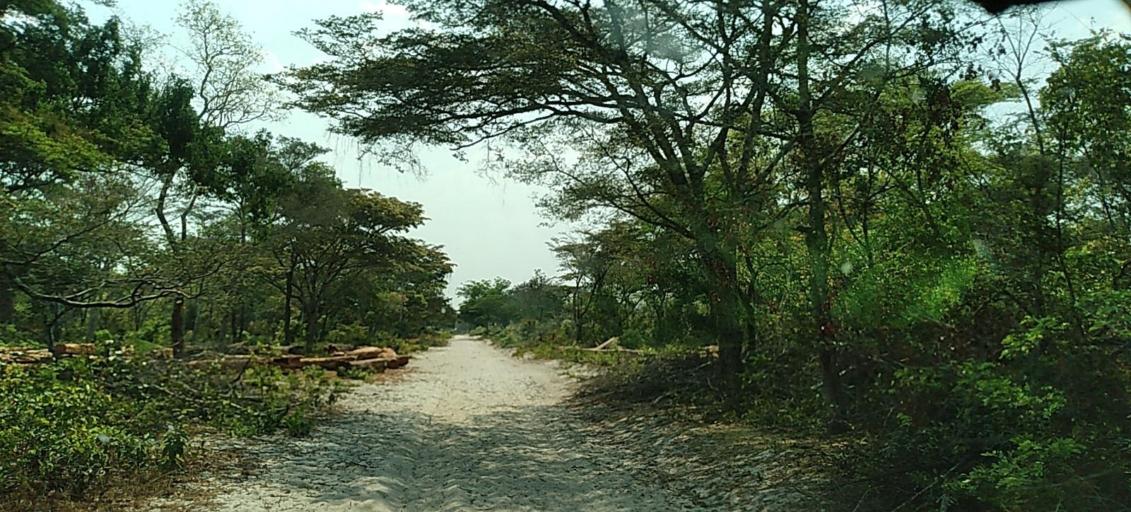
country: ZM
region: North-Western
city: Kabompo
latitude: -13.3869
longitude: 23.7723
